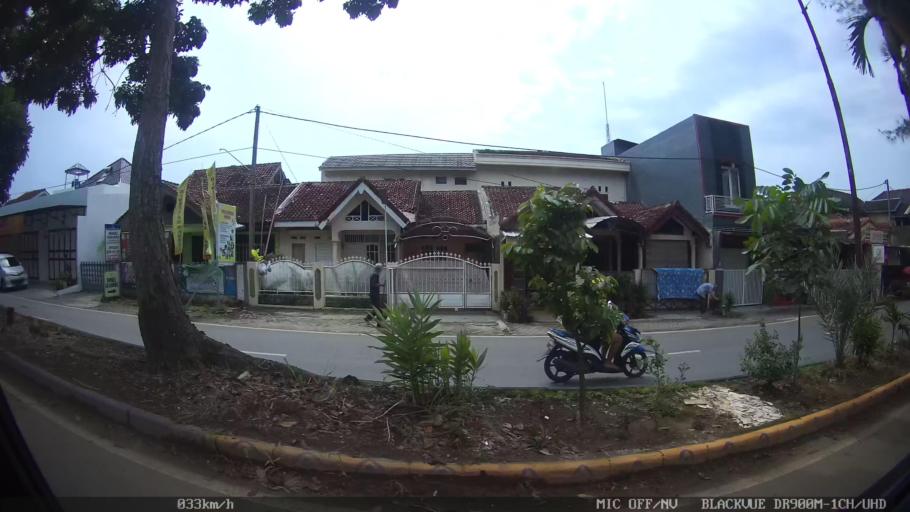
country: ID
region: Lampung
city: Bandarlampung
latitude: -5.4032
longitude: 105.2011
